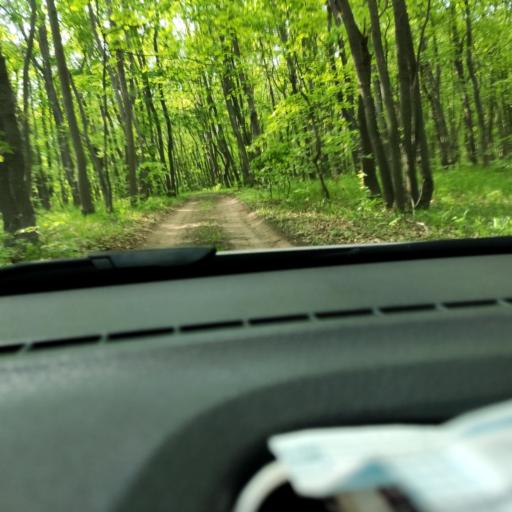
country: RU
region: Voronezj
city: Ramon'
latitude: 51.9431
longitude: 39.3699
